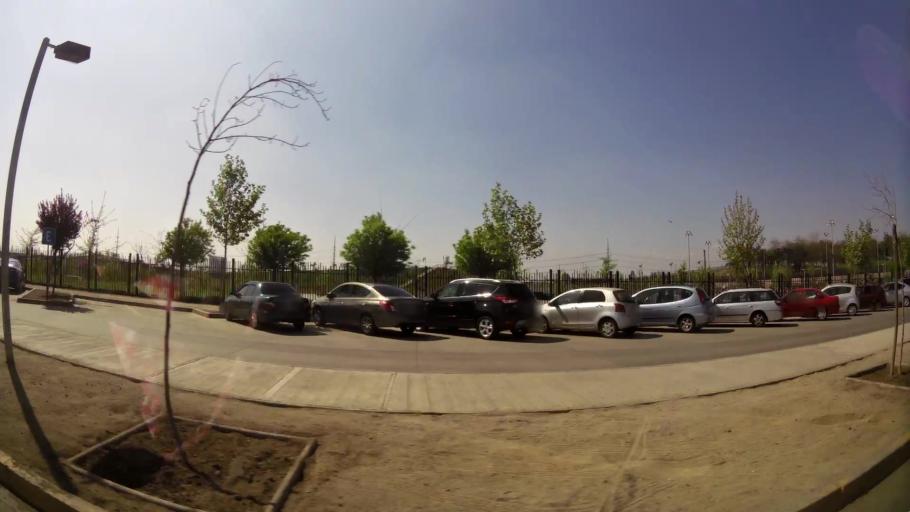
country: CL
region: Santiago Metropolitan
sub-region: Provincia de Santiago
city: Santiago
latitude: -33.4255
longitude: -70.6788
